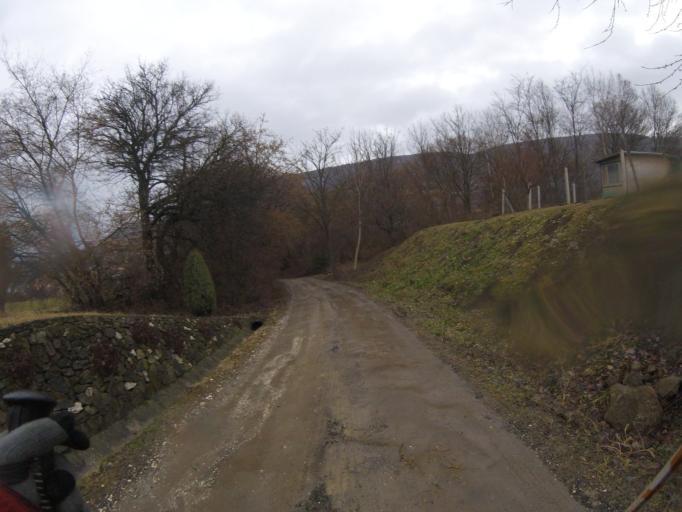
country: HU
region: Komarom-Esztergom
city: Kesztolc
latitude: 47.7099
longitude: 18.8041
